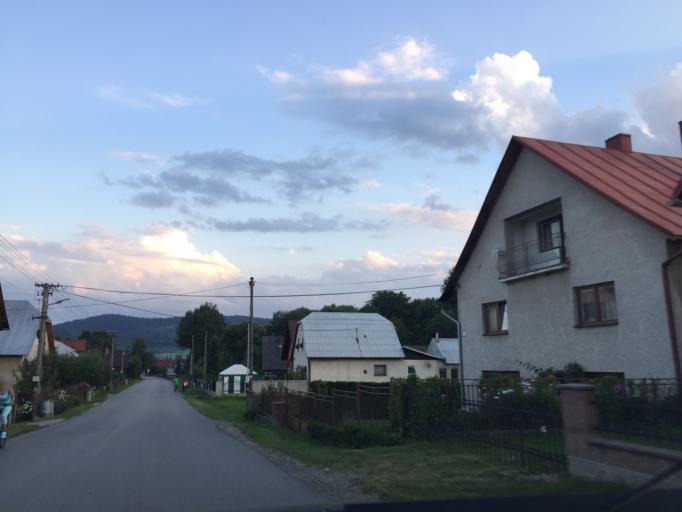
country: PL
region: Silesian Voivodeship
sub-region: Powiat zywiecki
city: Korbielow
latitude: 49.4641
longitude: 19.3834
